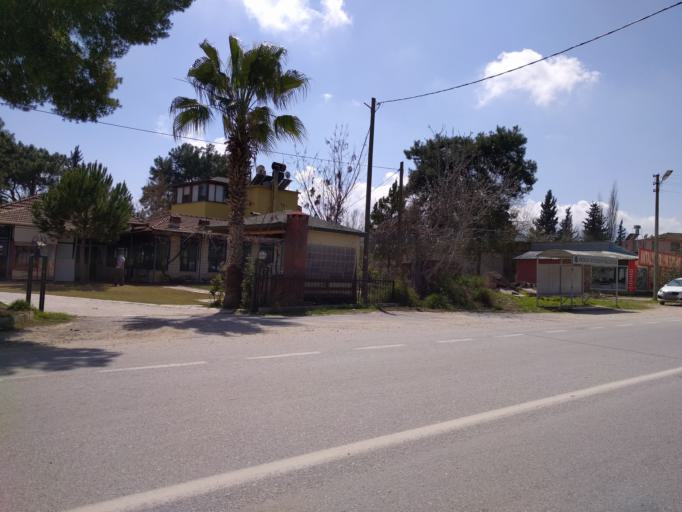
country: TR
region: Antalya
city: Cakirlar
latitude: 36.8947
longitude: 30.5964
